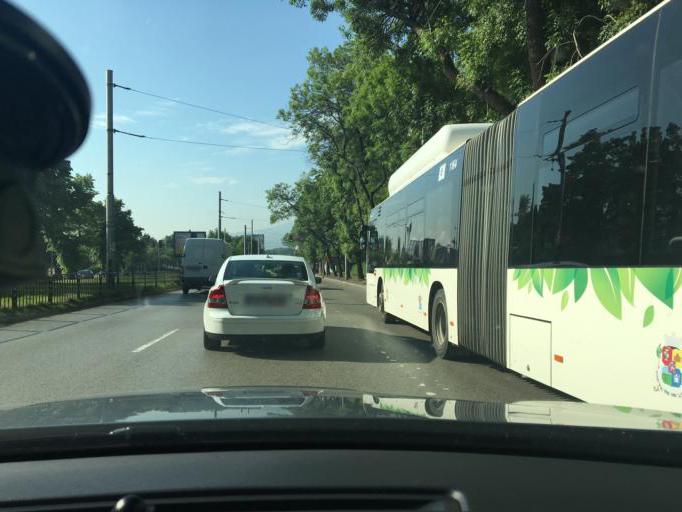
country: BG
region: Sofia-Capital
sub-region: Stolichna Obshtina
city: Sofia
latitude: 42.6819
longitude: 23.3016
